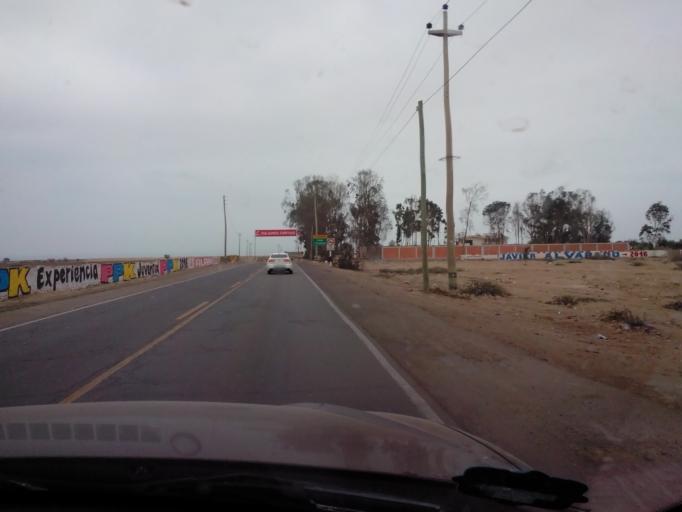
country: PE
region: Ica
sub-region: Provincia de Chincha
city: Sunampe
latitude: -13.4131
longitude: -76.1821
